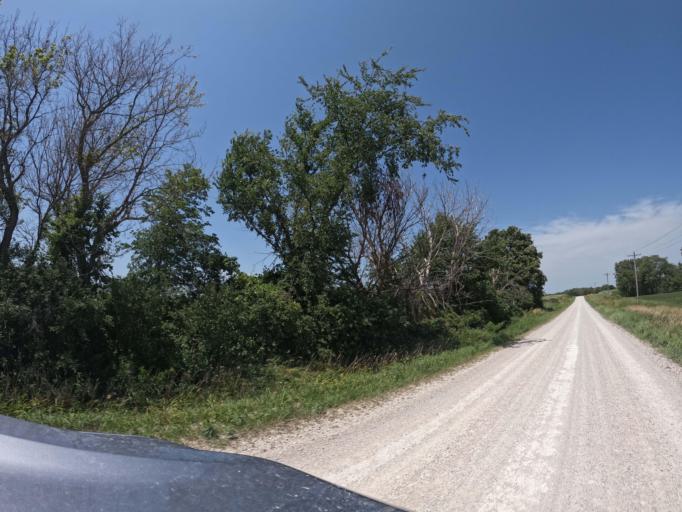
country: US
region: Iowa
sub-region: Henry County
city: Mount Pleasant
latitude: 40.9481
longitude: -91.6604
